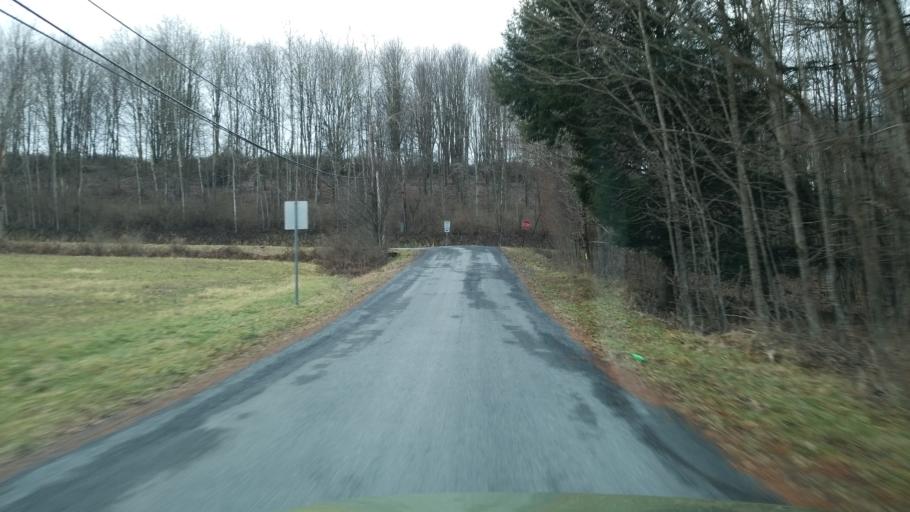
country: US
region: Pennsylvania
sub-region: Jefferson County
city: Falls Creek
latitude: 41.1790
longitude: -78.8140
